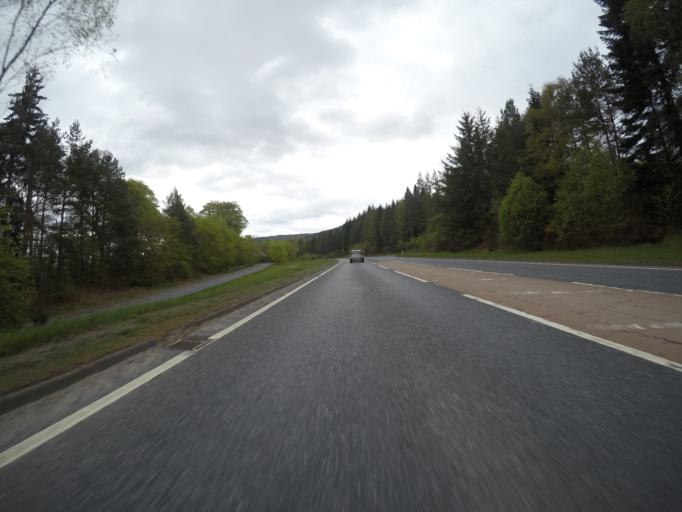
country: GB
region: Scotland
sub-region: Perth and Kinross
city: Pitlochry
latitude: 56.7027
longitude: -3.7510
